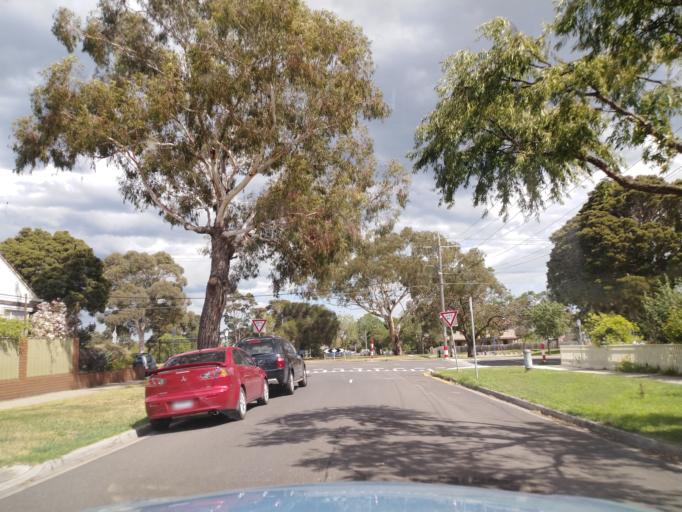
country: AU
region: Victoria
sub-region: Hobsons Bay
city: Newport
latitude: -37.8396
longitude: 144.8780
